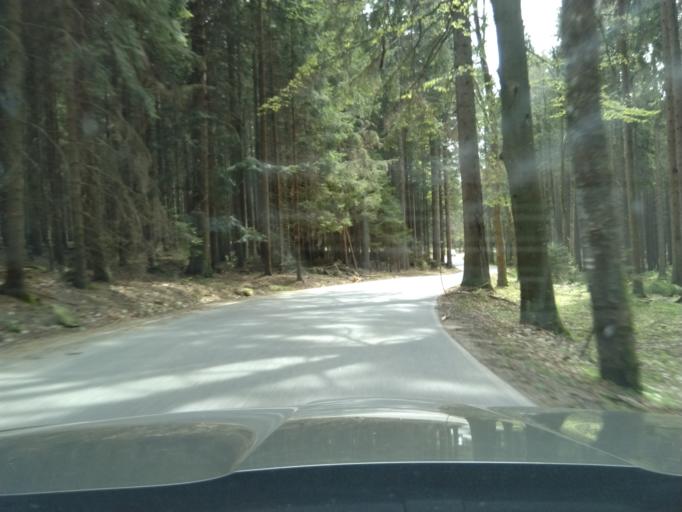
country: CZ
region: Jihocesky
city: Vacov
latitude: 49.1557
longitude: 13.6930
